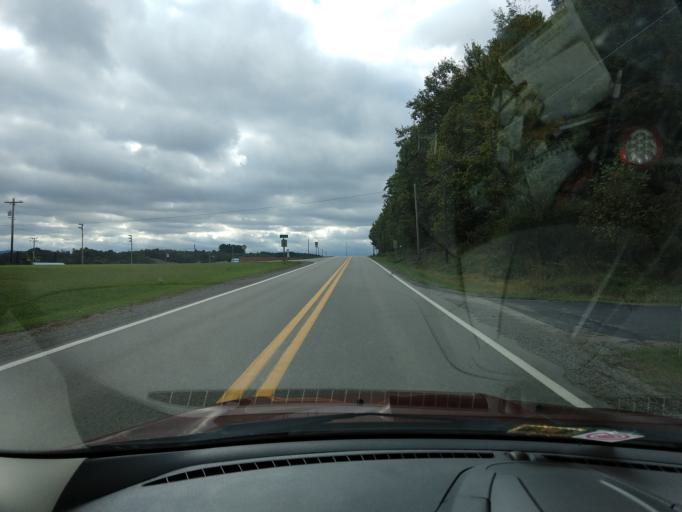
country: US
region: West Virginia
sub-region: Barbour County
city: Philippi
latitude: 39.1135
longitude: -79.9955
